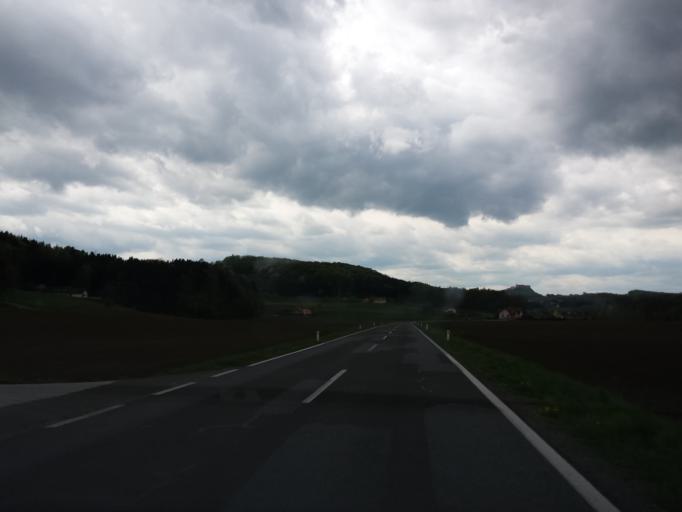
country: AT
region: Styria
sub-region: Politischer Bezirk Suedoststeiermark
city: Hatzendorf
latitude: 46.9869
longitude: 15.9850
